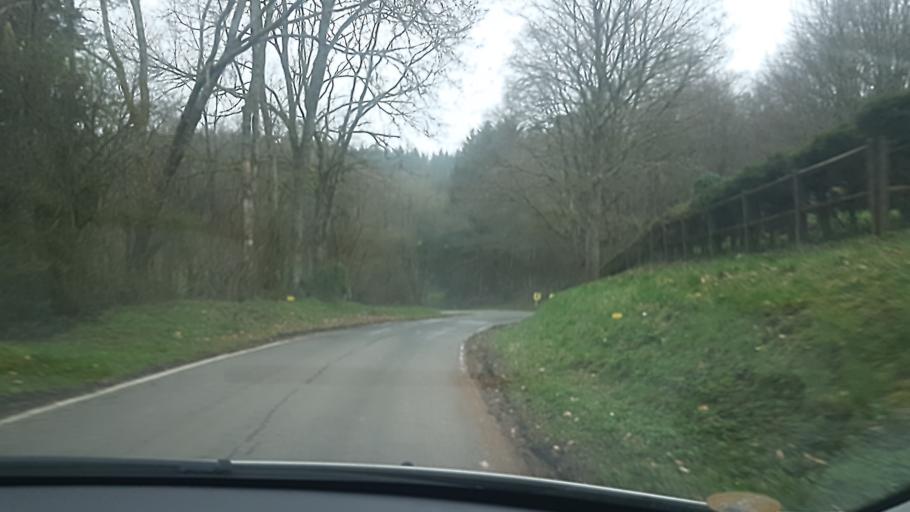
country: FR
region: Champagne-Ardenne
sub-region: Departement des Ardennes
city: Haybes
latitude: 50.0312
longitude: 4.6679
